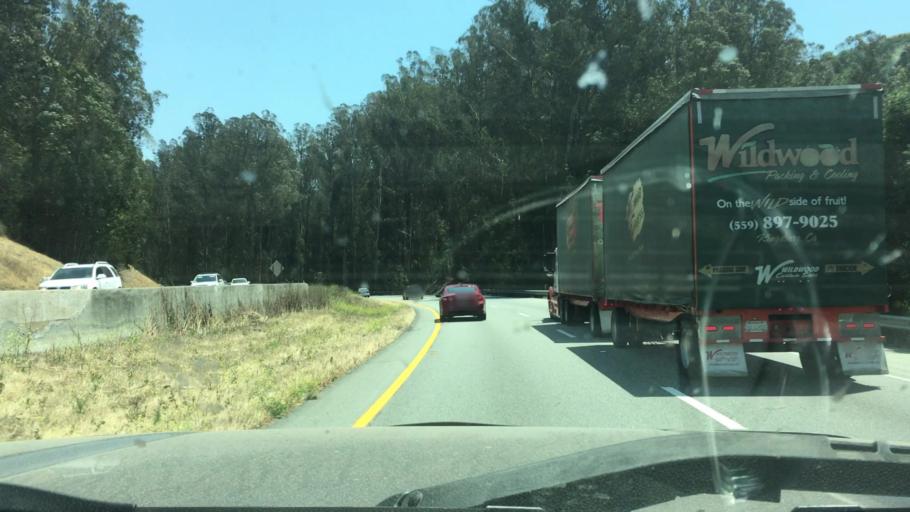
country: US
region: California
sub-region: San Benito County
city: Aromas
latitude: 36.8652
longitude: -121.6415
